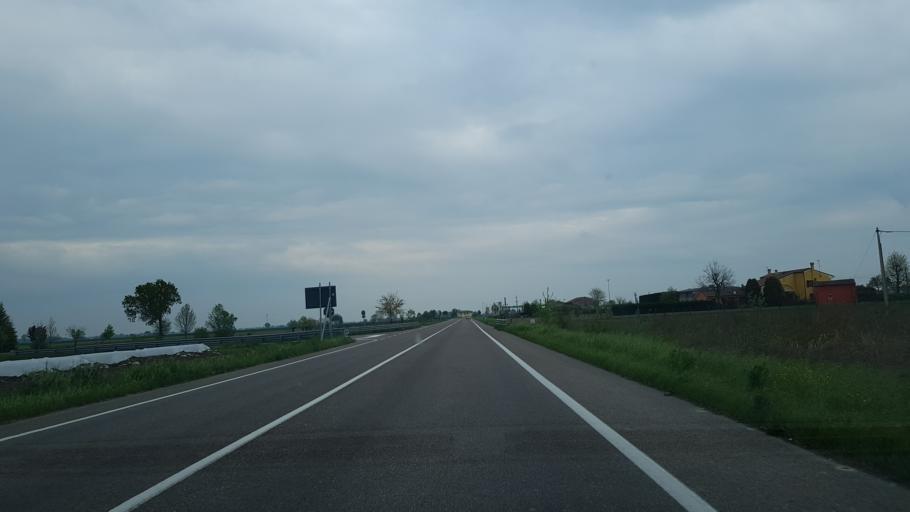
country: IT
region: Veneto
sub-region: Provincia di Rovigo
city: Melara
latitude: 45.0776
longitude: 11.2048
